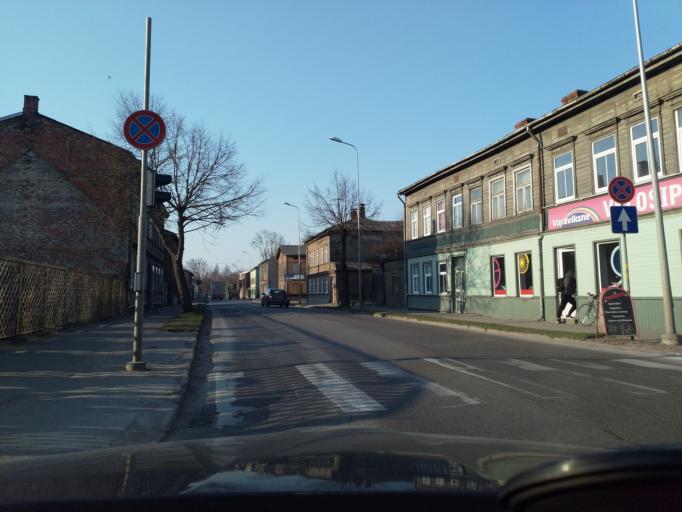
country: LV
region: Liepaja
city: Liepaja
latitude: 56.5006
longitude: 21.0173
